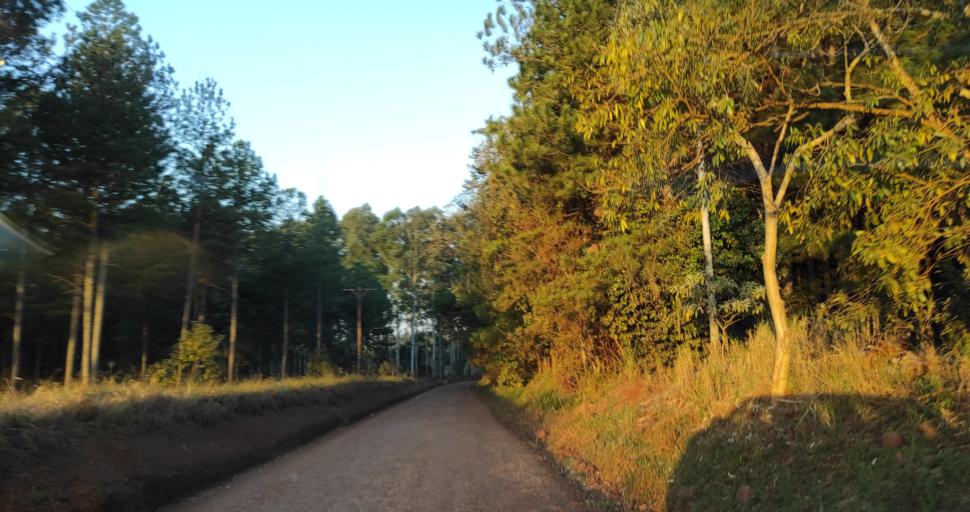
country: AR
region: Misiones
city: Capiovi
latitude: -26.8733
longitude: -55.1054
